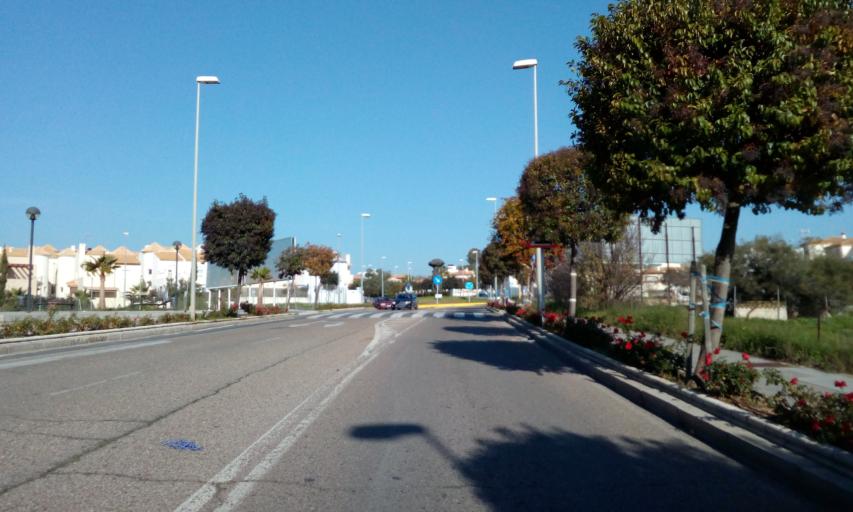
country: ES
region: Andalusia
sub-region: Provincia de Huelva
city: Ayamonte
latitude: 37.2219
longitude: -7.4011
